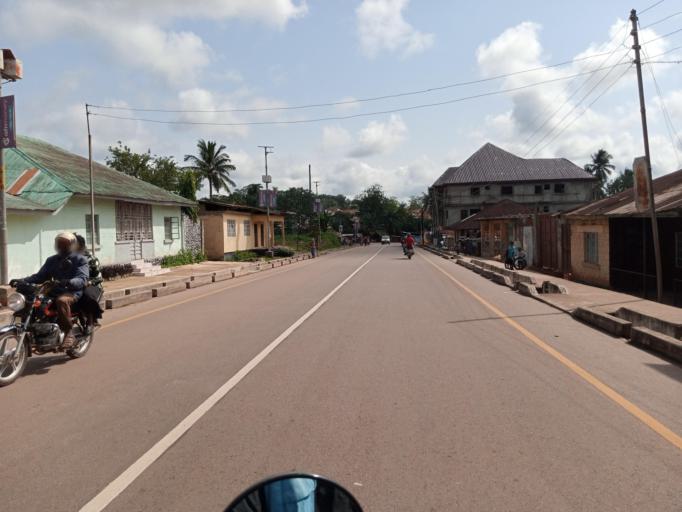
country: SL
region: Southern Province
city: Bo
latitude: 7.9717
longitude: -11.7381
